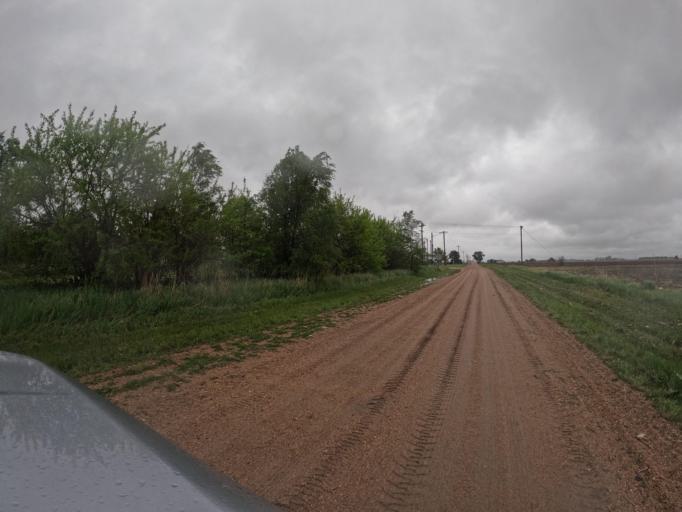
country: US
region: Nebraska
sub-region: Clay County
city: Harvard
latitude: 40.6159
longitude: -98.1027
